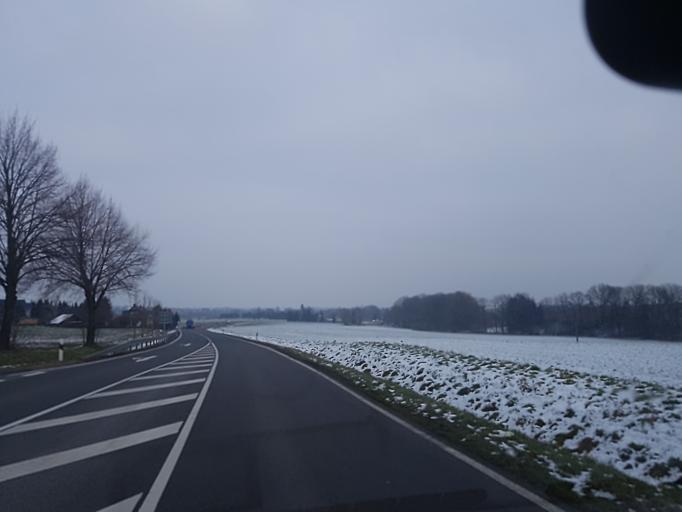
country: DE
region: Saxony
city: Mugeln
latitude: 51.2296
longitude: 13.0217
